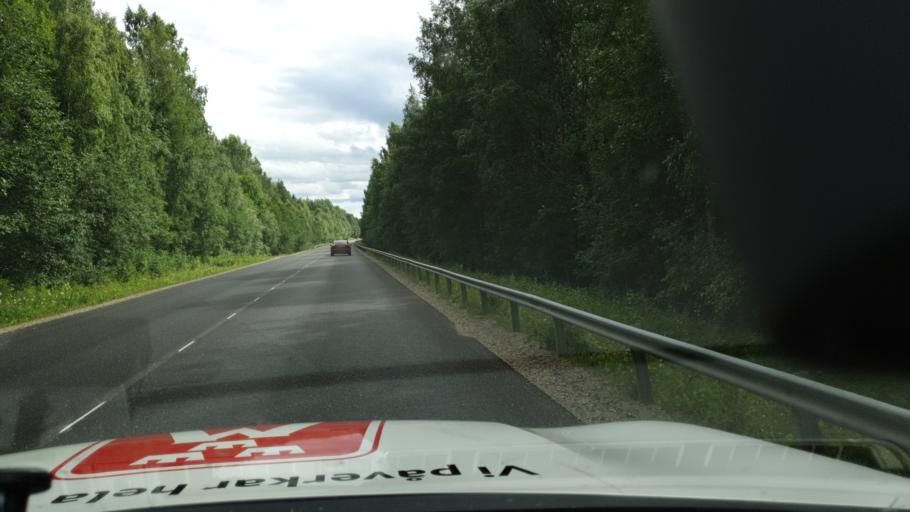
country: SE
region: Vaesterbotten
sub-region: Vindelns Kommun
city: Vindeln
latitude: 64.3021
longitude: 19.6154
